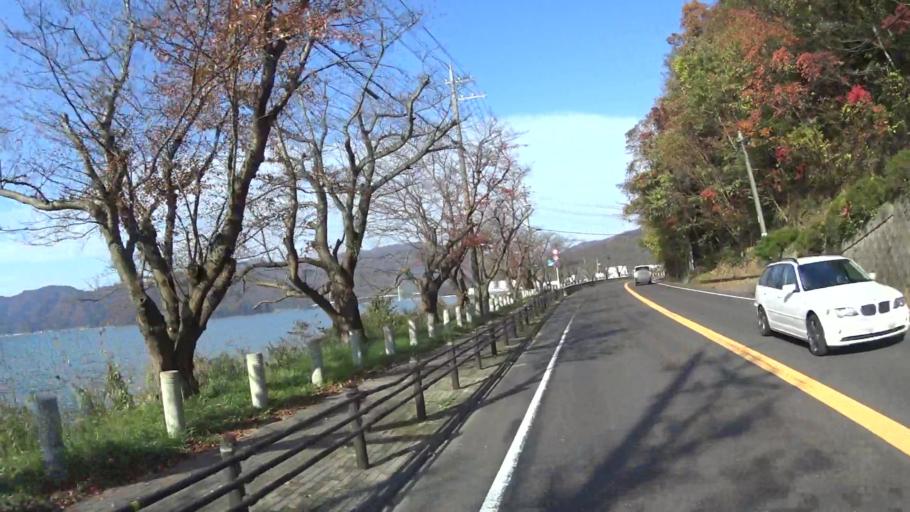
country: JP
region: Kyoto
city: Maizuru
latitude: 35.4888
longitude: 135.3959
